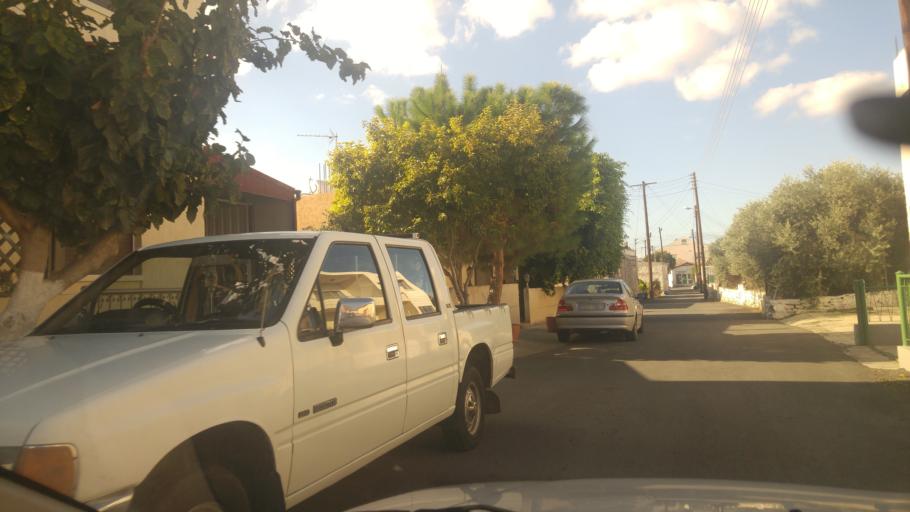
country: CY
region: Limassol
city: Ypsonas
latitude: 34.6887
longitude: 32.9626
